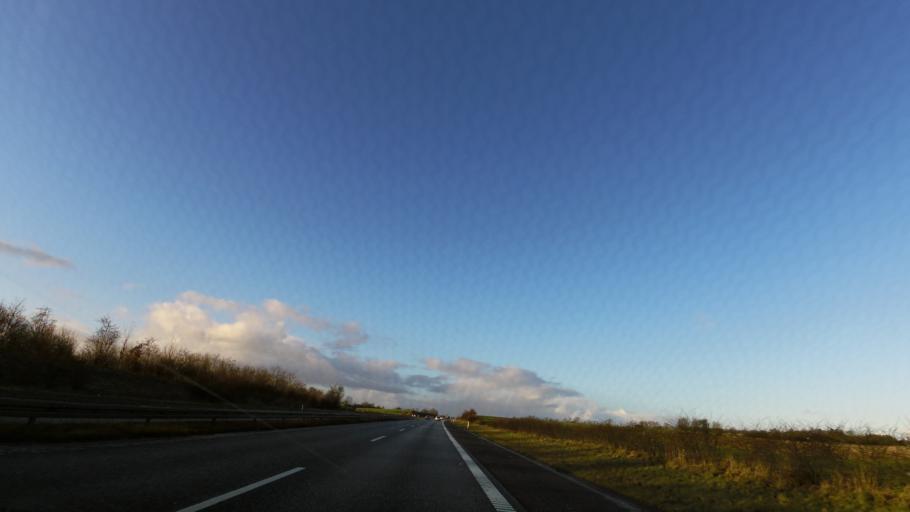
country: DK
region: Central Jutland
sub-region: Skanderborg Kommune
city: Galten
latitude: 56.1439
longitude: 9.8914
